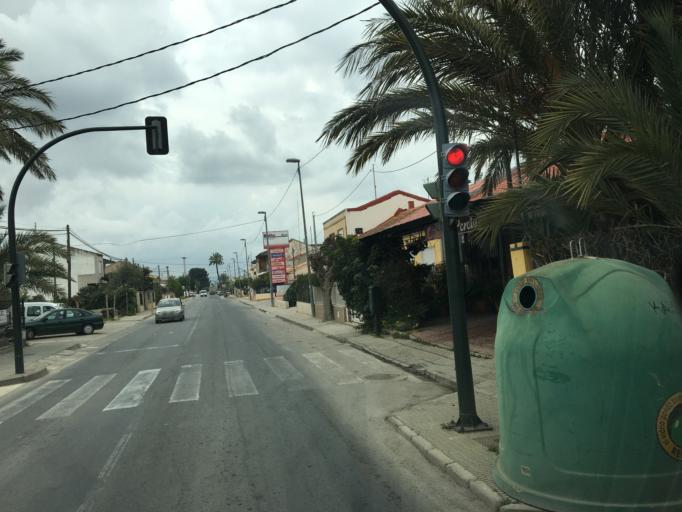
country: ES
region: Murcia
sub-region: Murcia
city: Beniel
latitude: 38.0252
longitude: -1.0297
